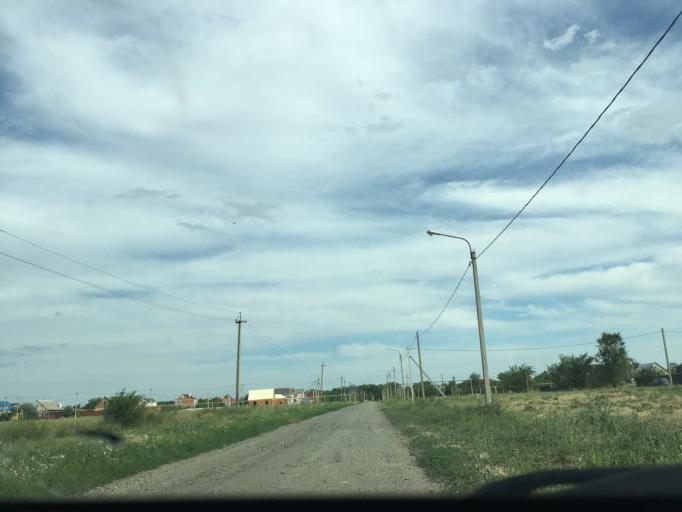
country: RU
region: Krasnodarskiy
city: Kushchevskaya
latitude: 46.5526
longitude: 39.6685
